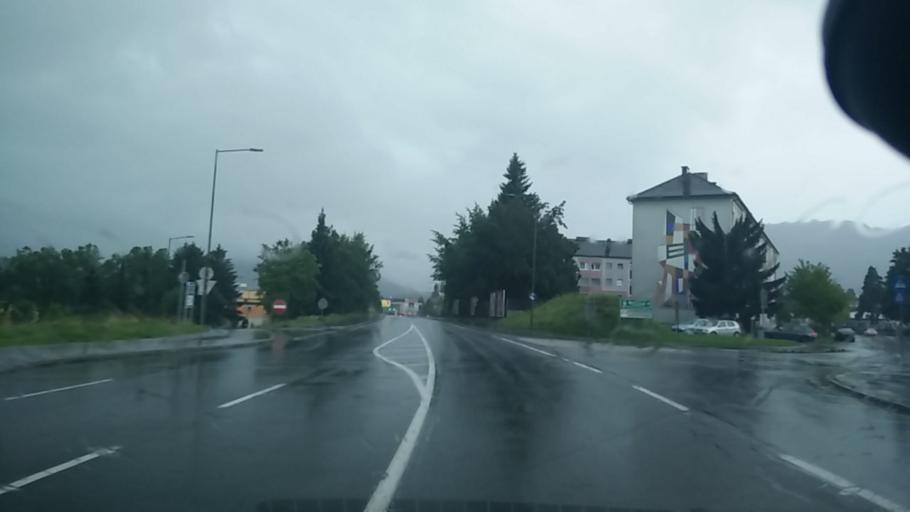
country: AT
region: Carinthia
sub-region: Villach Stadt
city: Villach
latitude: 46.6038
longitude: 13.8429
